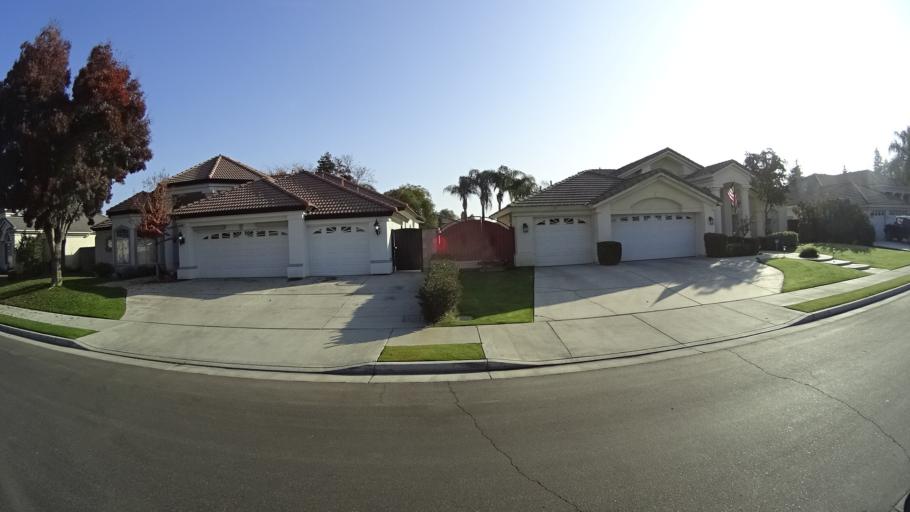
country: US
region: California
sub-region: Kern County
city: Greenacres
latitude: 35.3662
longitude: -119.1240
